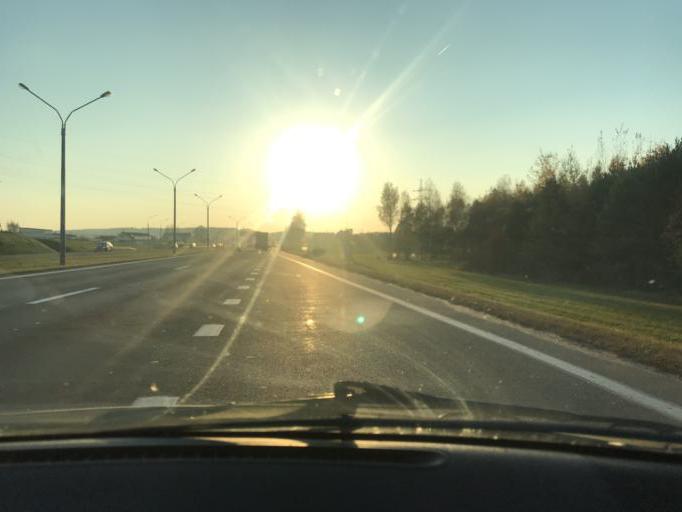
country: BY
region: Minsk
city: Korolev Stan
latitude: 53.9926
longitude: 27.8085
